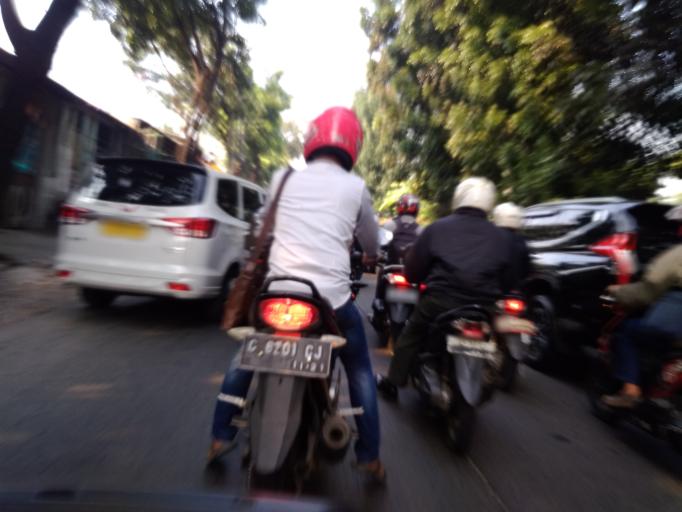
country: ID
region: Jakarta Raya
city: Jakarta
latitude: -6.3007
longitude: 106.8403
